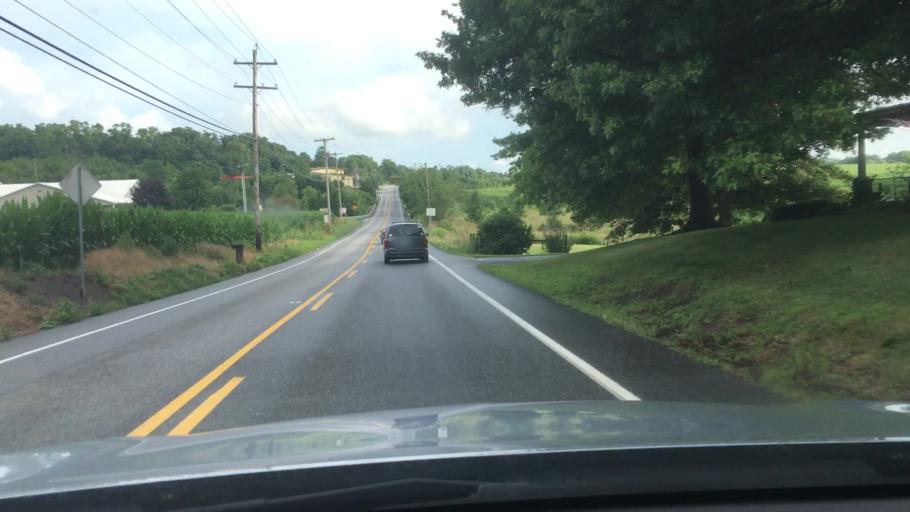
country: US
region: Pennsylvania
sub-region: York County
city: Dillsburg
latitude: 40.1246
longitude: -77.0363
